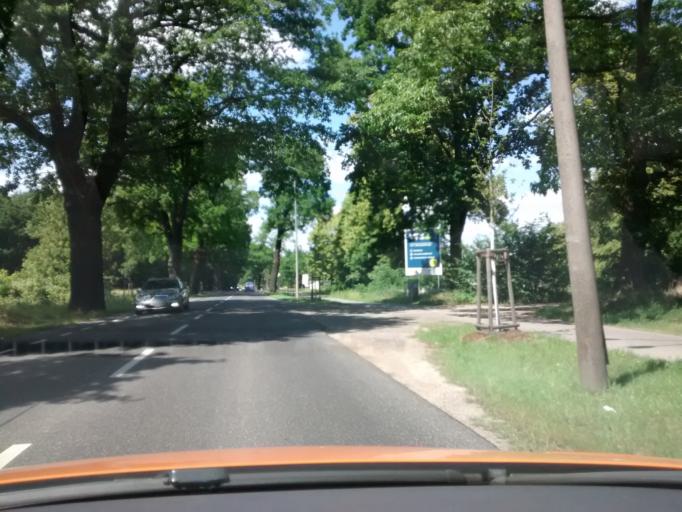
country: DE
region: Brandenburg
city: Potsdam
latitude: 52.4318
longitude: 13.0537
